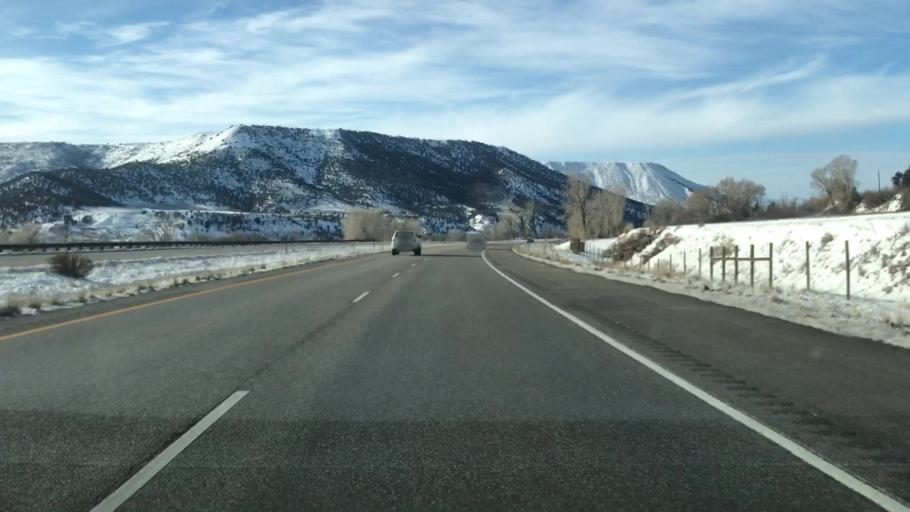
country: US
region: Colorado
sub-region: Garfield County
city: New Castle
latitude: 39.5603
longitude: -107.5553
